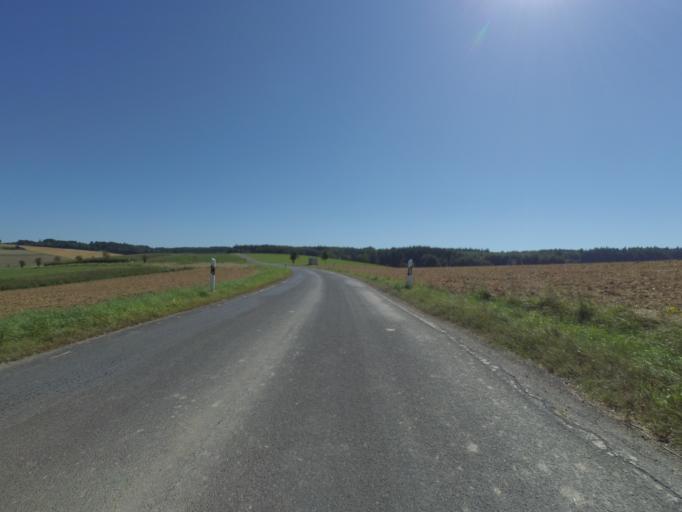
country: DE
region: Rheinland-Pfalz
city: Gillenbeuren
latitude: 50.1612
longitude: 7.0239
